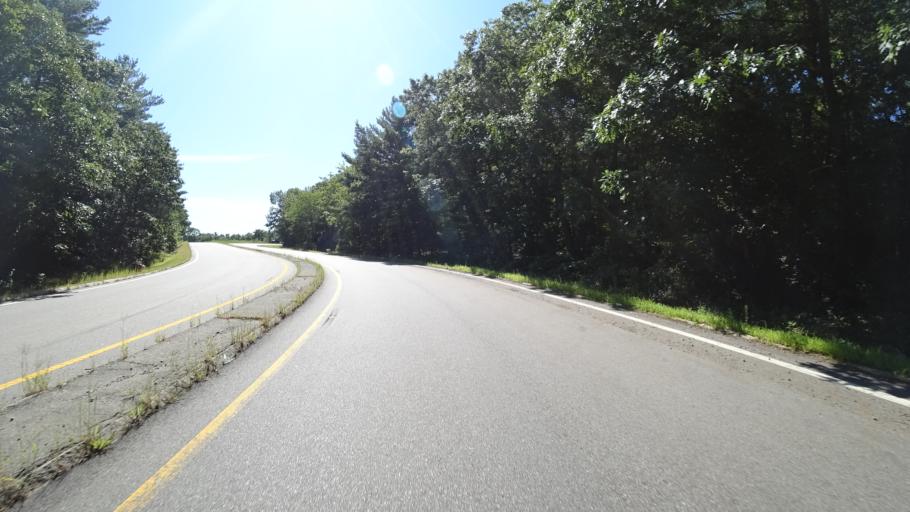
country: US
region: Massachusetts
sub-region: Norfolk County
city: Needham
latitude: 42.2647
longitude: -71.2100
